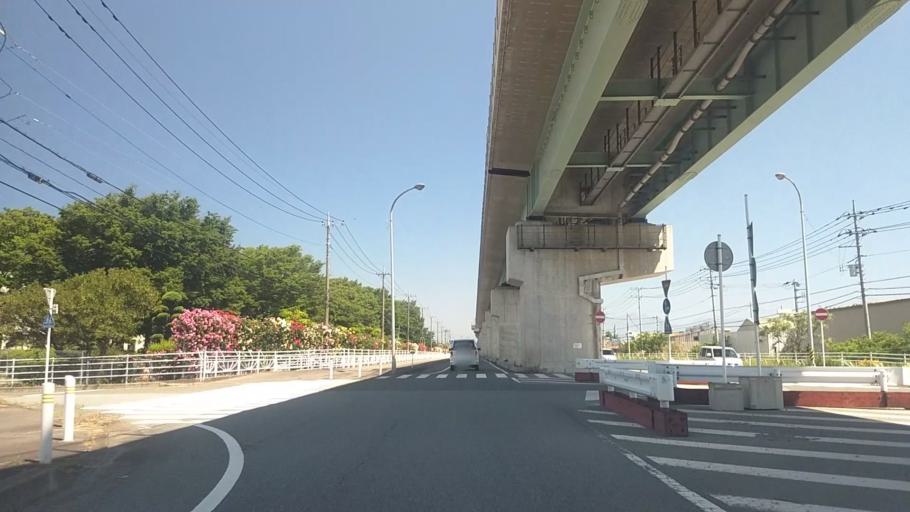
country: JP
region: Yamanashi
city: Ryuo
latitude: 35.5782
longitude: 138.4753
